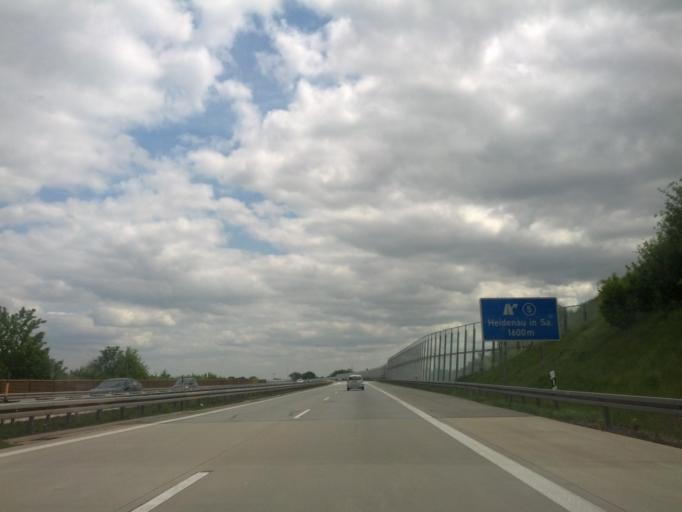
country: DE
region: Saxony
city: Kreischa
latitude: 50.9823
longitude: 13.7885
